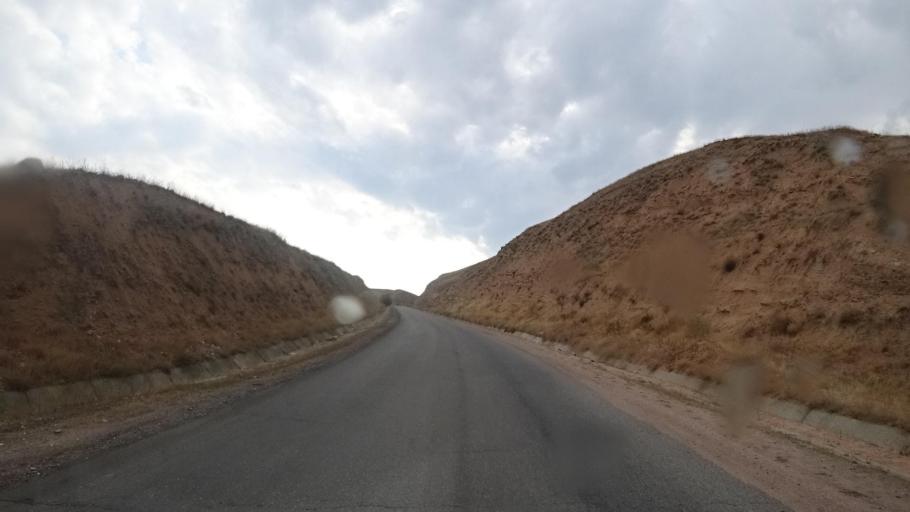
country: KG
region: Jalal-Abad
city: Toktogul
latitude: 41.8595
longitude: 73.0347
